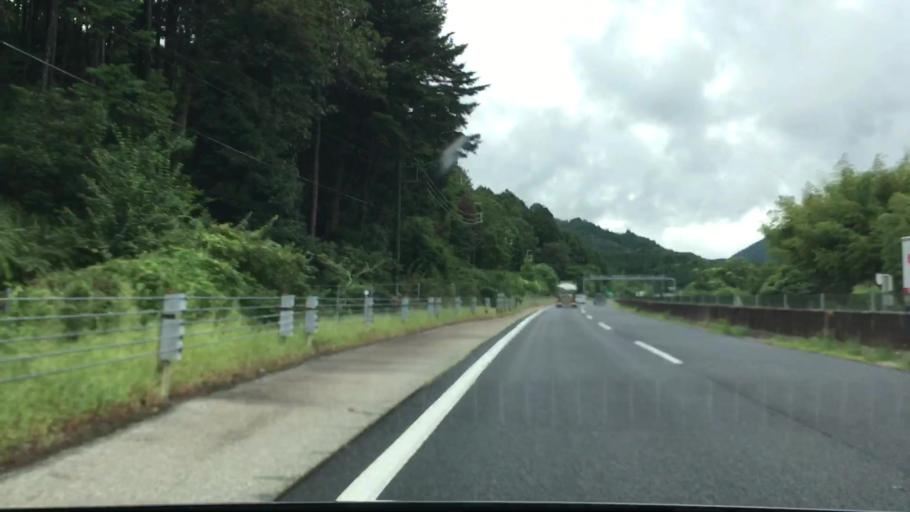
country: JP
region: Hyogo
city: Yamazakicho-nakabirose
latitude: 35.0221
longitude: 134.4969
